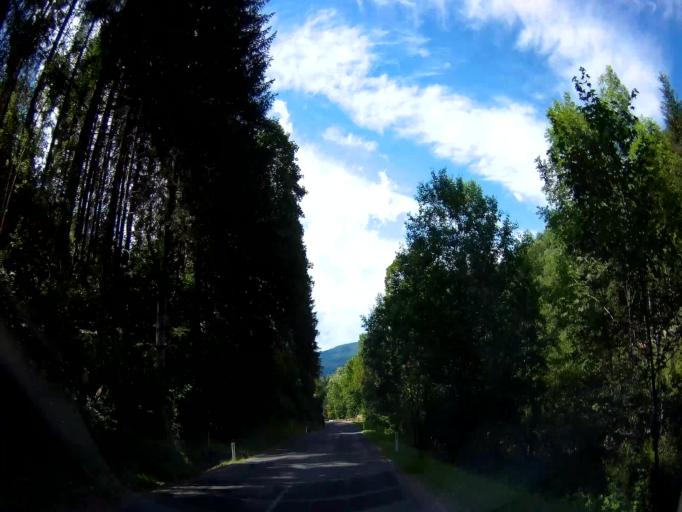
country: AT
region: Styria
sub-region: Politischer Bezirk Murau
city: Stadl an der Mur
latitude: 47.0537
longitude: 13.9959
